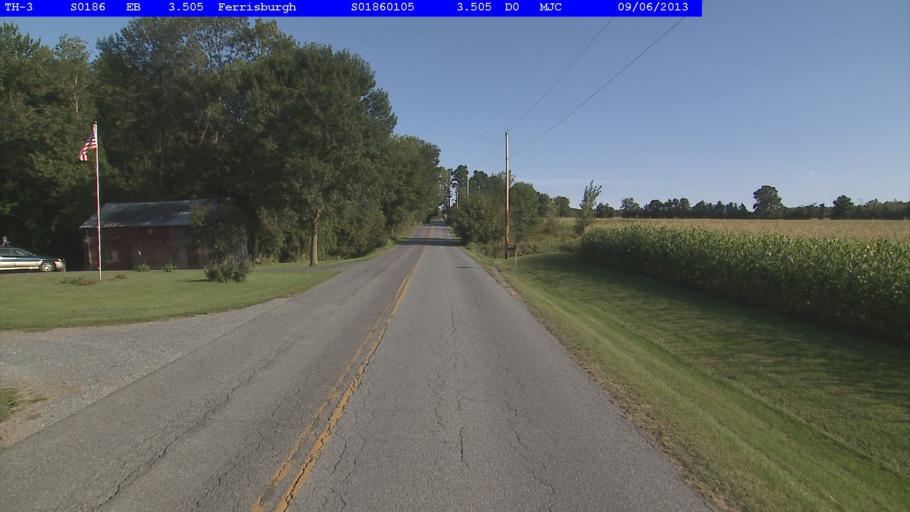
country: US
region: Vermont
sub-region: Addison County
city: Vergennes
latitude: 44.1763
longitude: -73.3073
